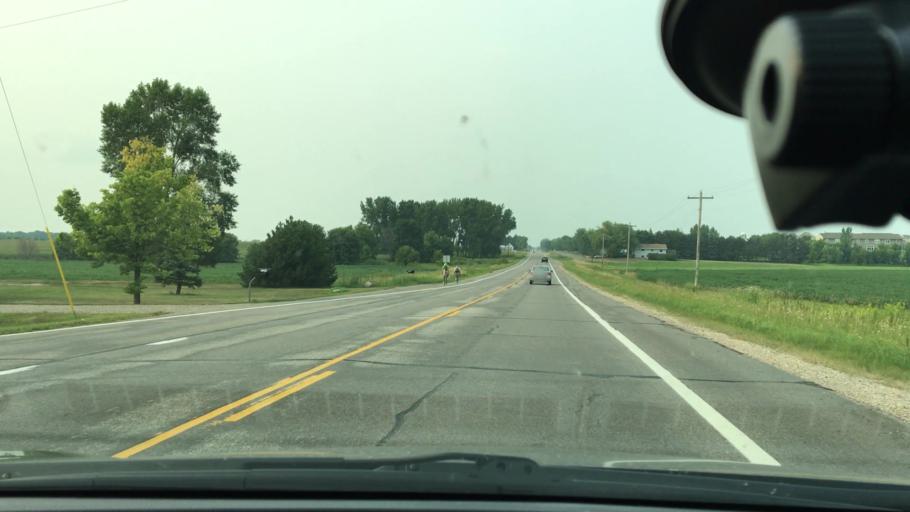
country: US
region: Minnesota
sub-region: Wright County
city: Albertville
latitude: 45.2565
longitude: -93.6633
